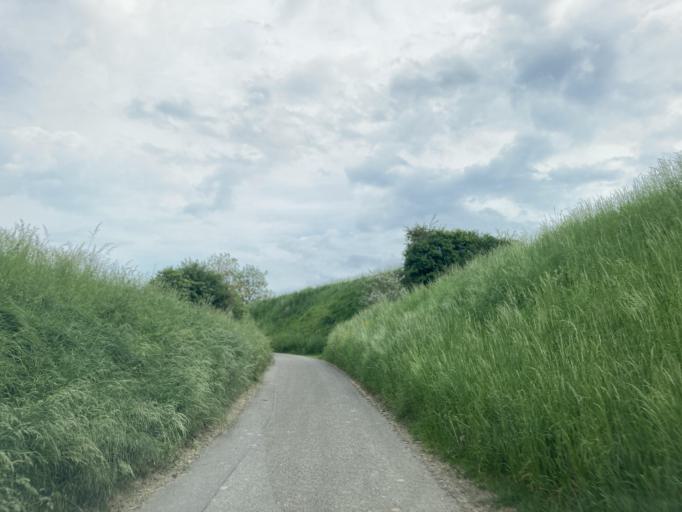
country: DE
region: Baden-Wuerttemberg
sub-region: Freiburg Region
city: Bahlingen
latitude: 48.1122
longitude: 7.7182
